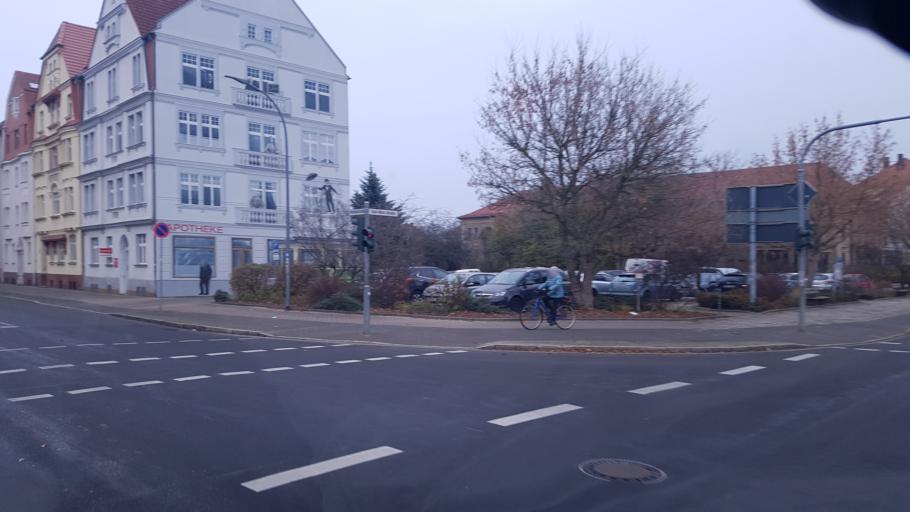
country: DE
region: Brandenburg
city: Guben
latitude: 51.9476
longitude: 14.7035
